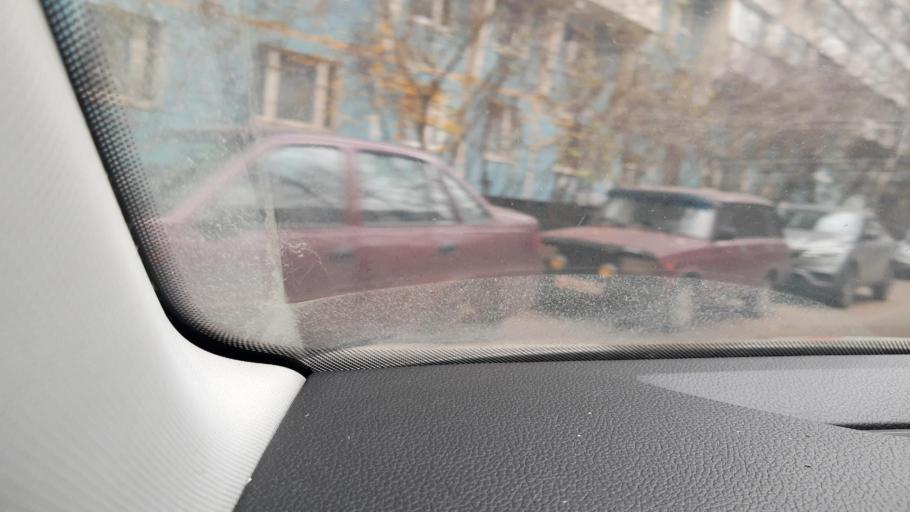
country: RU
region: Moscow
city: Biryulevo
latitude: 55.5843
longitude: 37.6887
